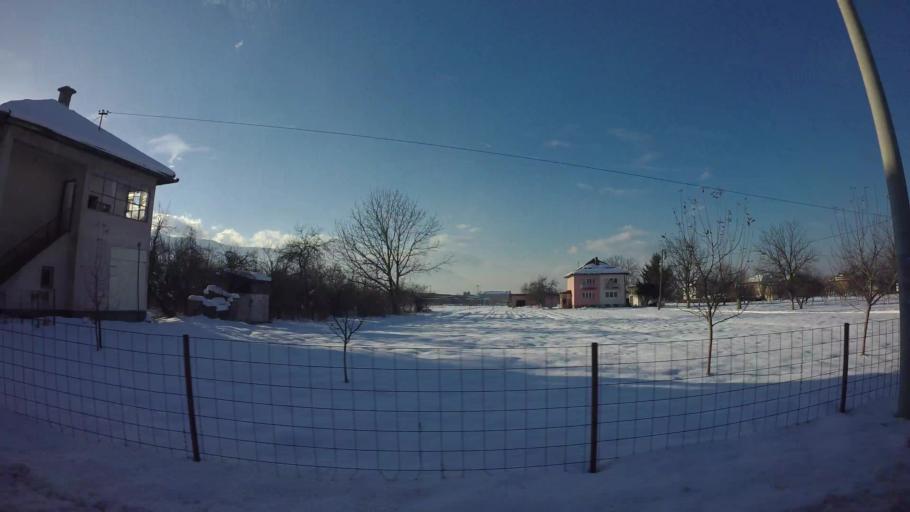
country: BA
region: Federation of Bosnia and Herzegovina
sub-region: Kanton Sarajevo
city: Sarajevo
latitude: 43.8143
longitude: 18.3465
